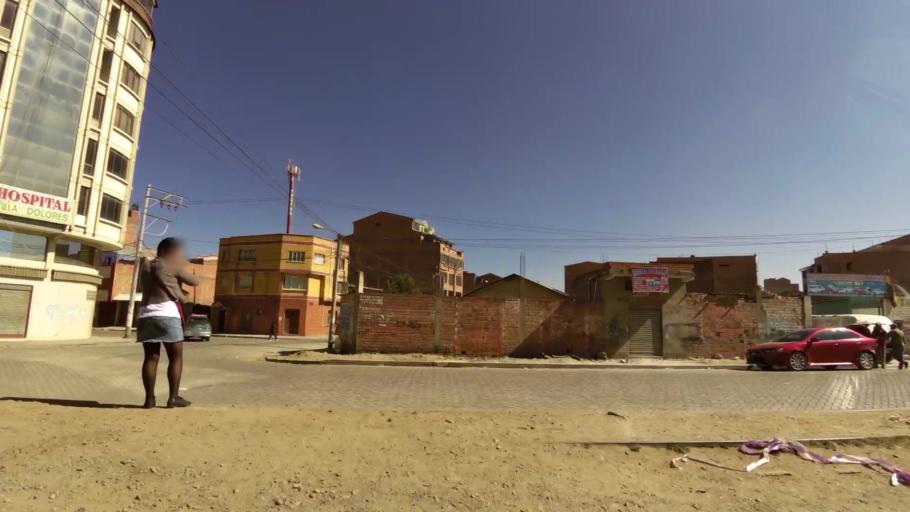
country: BO
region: La Paz
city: La Paz
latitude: -16.5162
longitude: -68.1559
